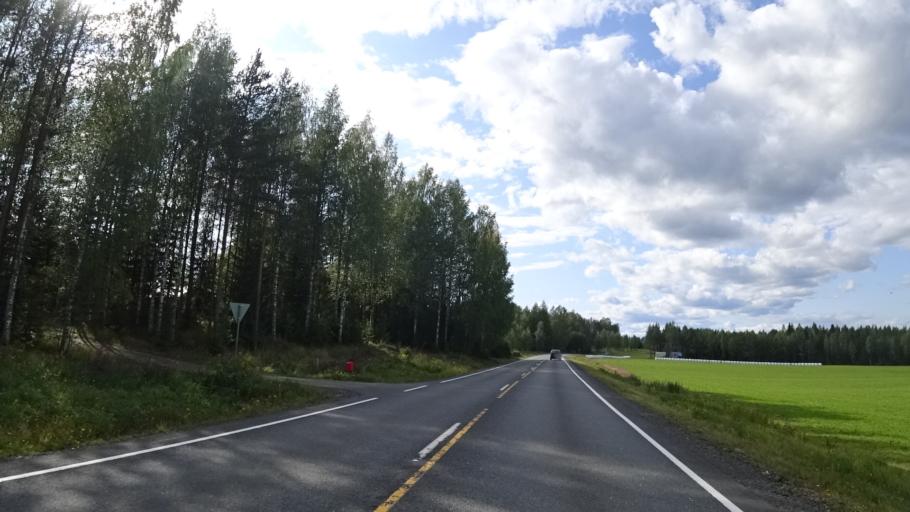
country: FI
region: North Karelia
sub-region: Keski-Karjala
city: Tohmajaervi
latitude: 62.1903
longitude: 30.4391
